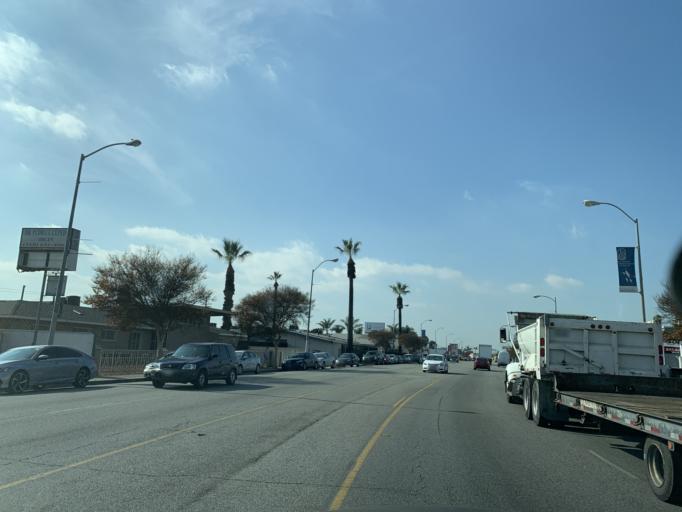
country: US
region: California
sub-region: Los Angeles County
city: Lynwood
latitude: 33.9305
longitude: -118.2054
